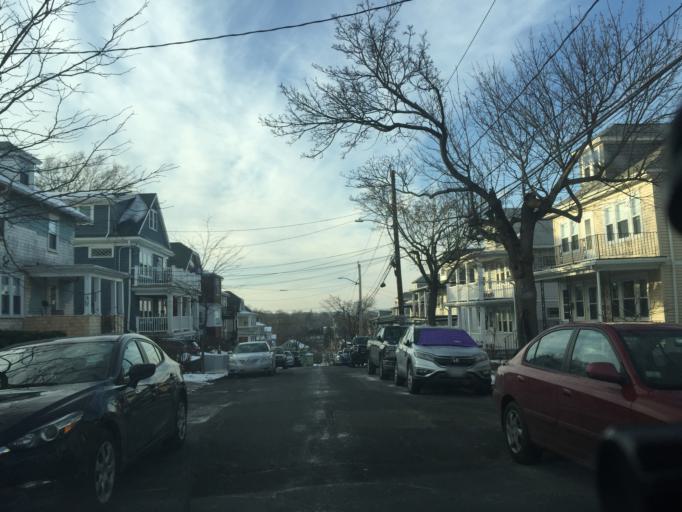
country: US
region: Massachusetts
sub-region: Middlesex County
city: Watertown
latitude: 42.3484
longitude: -71.1671
